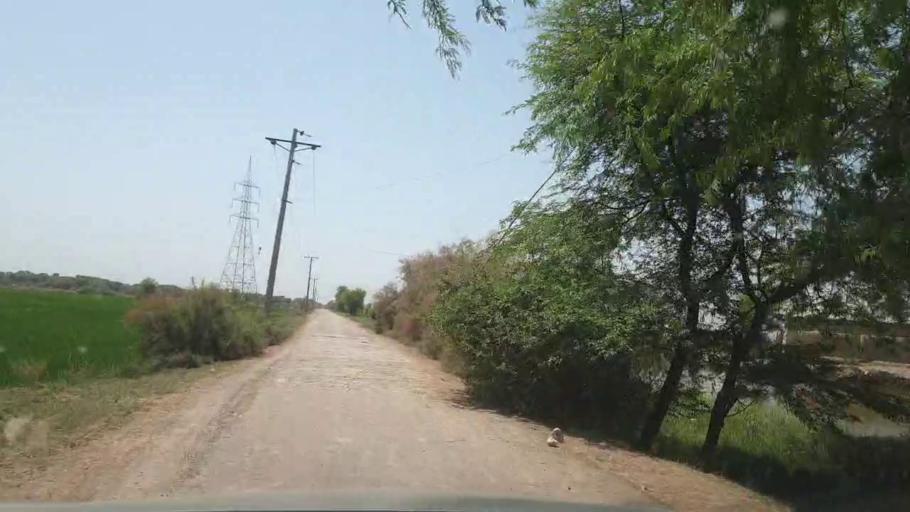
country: PK
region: Sindh
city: Warah
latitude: 27.4942
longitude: 67.7468
